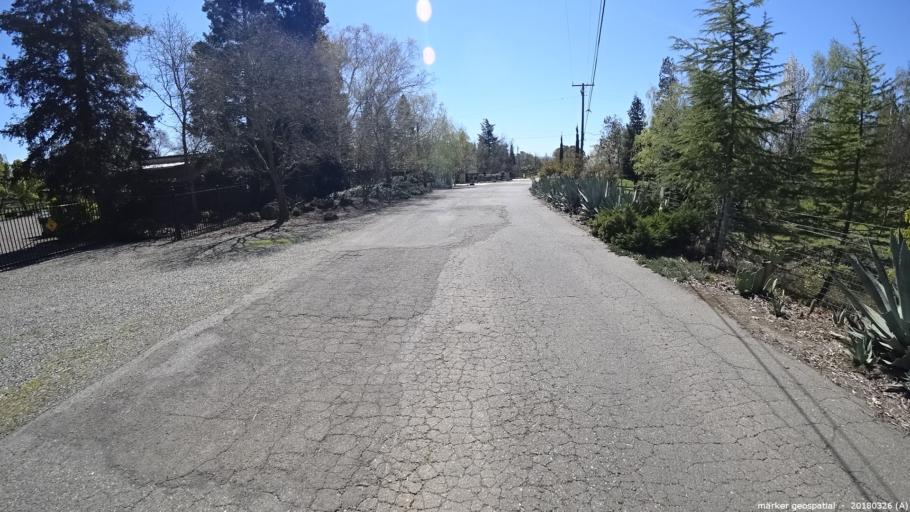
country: US
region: California
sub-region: Sacramento County
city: Wilton
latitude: 38.4580
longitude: -121.2819
